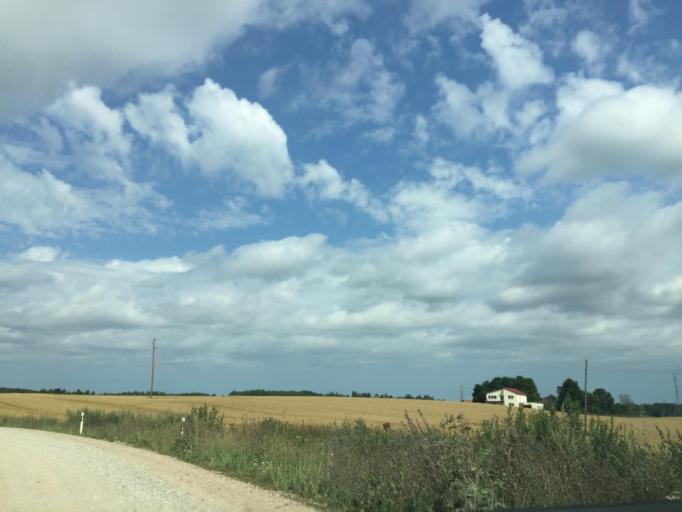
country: LV
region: Kandava
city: Kandava
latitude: 56.9989
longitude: 22.8660
